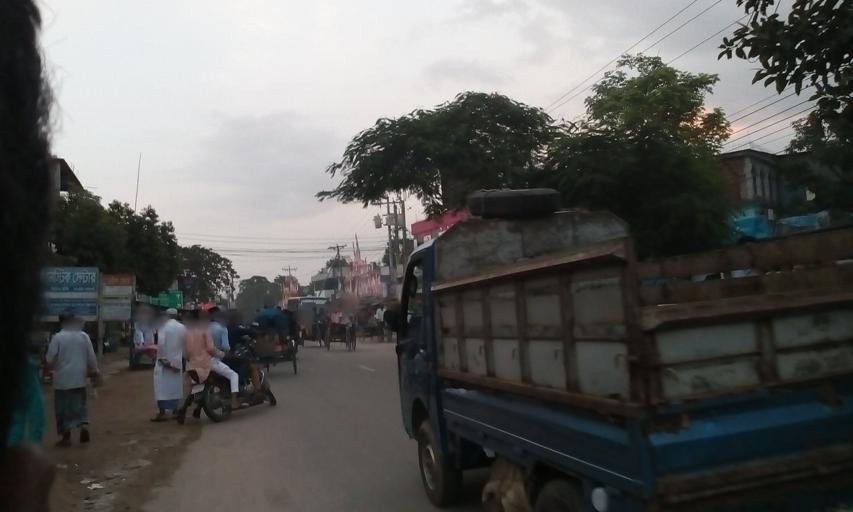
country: IN
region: West Bengal
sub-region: Dakshin Dinajpur
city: Balurghat
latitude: 25.3899
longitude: 88.9906
